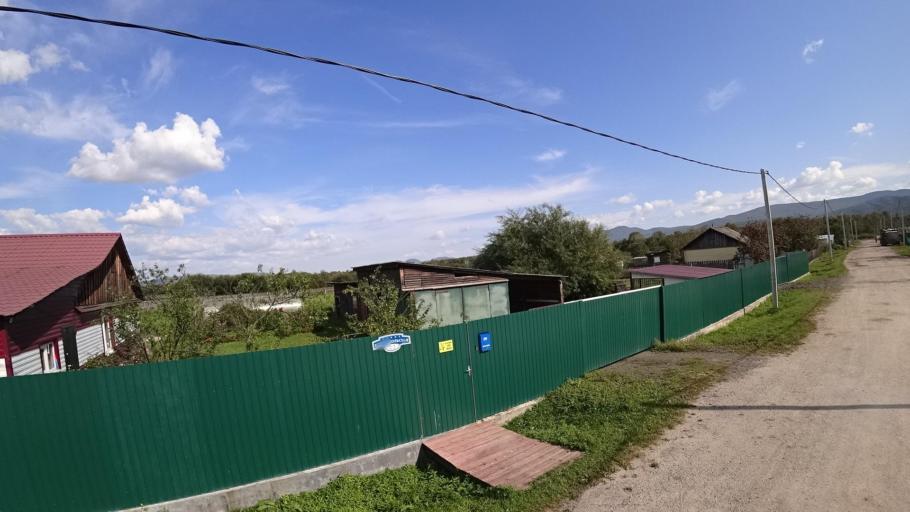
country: RU
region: Jewish Autonomous Oblast
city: Birakan
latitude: 48.9849
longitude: 131.7271
